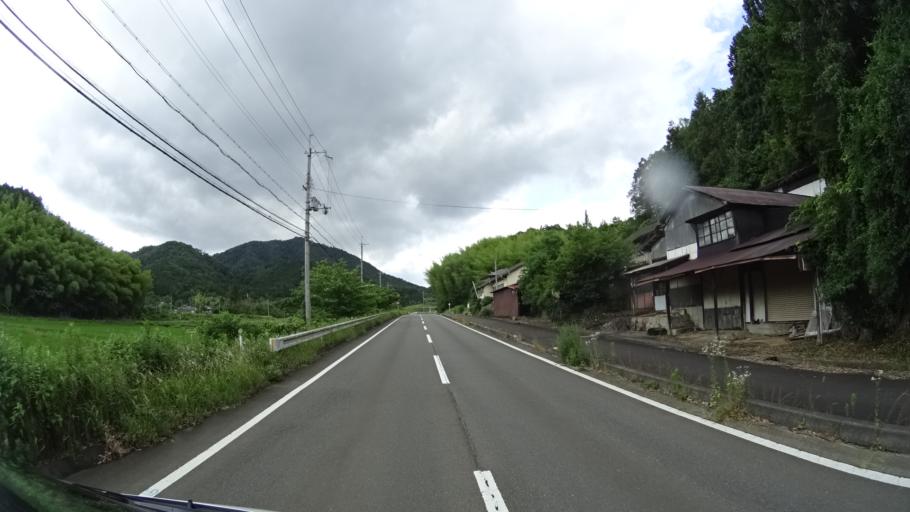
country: JP
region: Kyoto
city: Ayabe
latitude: 35.3322
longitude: 135.2063
